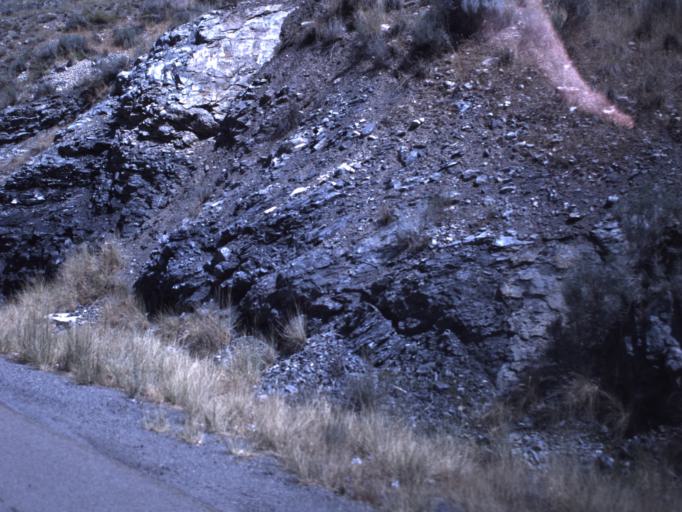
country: US
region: Utah
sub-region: Utah County
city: Orem
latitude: 40.3247
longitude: -111.6425
